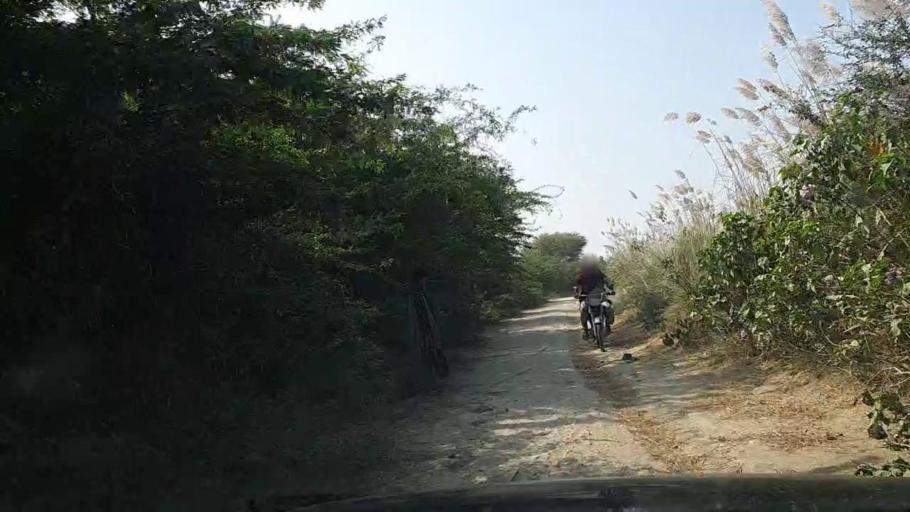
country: PK
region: Sindh
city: Gharo
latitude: 24.7042
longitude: 67.6463
